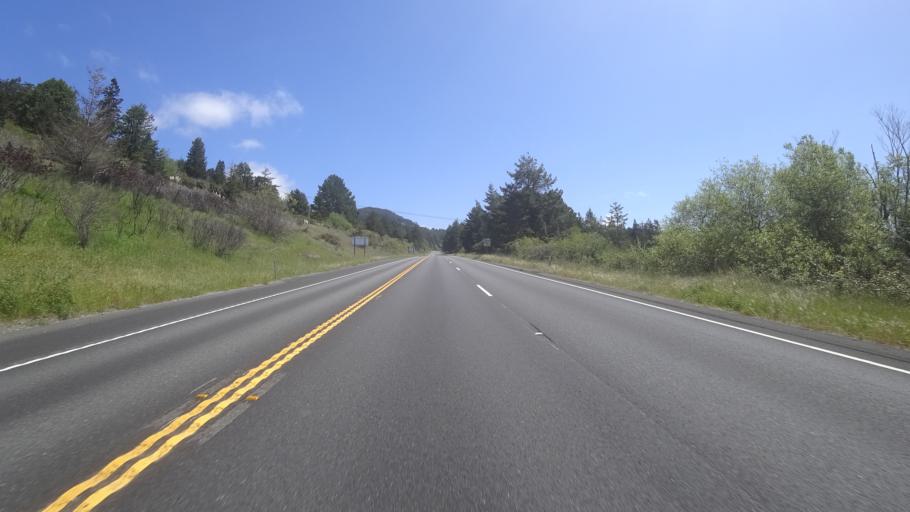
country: US
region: California
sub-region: Humboldt County
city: Blue Lake
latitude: 40.8873
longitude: -123.9872
